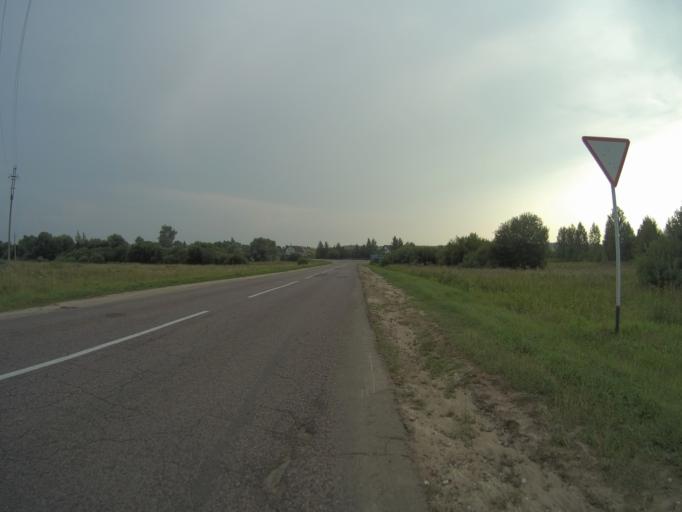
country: RU
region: Ivanovo
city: Gavrilov Posad
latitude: 56.3331
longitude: 40.1191
